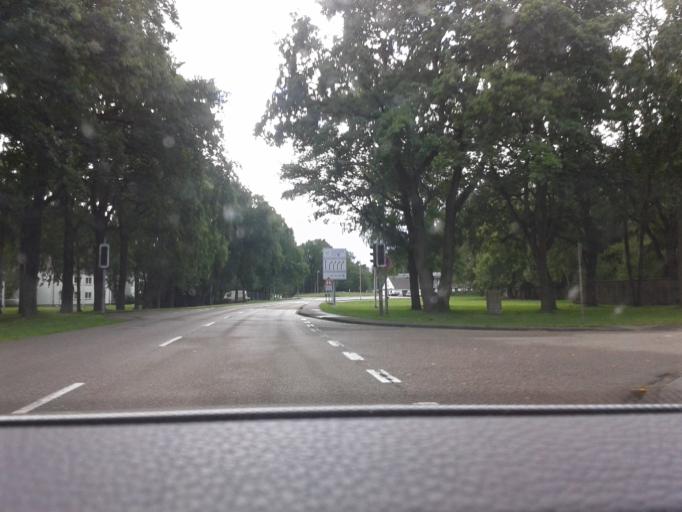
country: DE
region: North Rhine-Westphalia
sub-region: Regierungsbezirk Dusseldorf
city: Weeze
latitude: 51.5943
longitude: 6.1662
